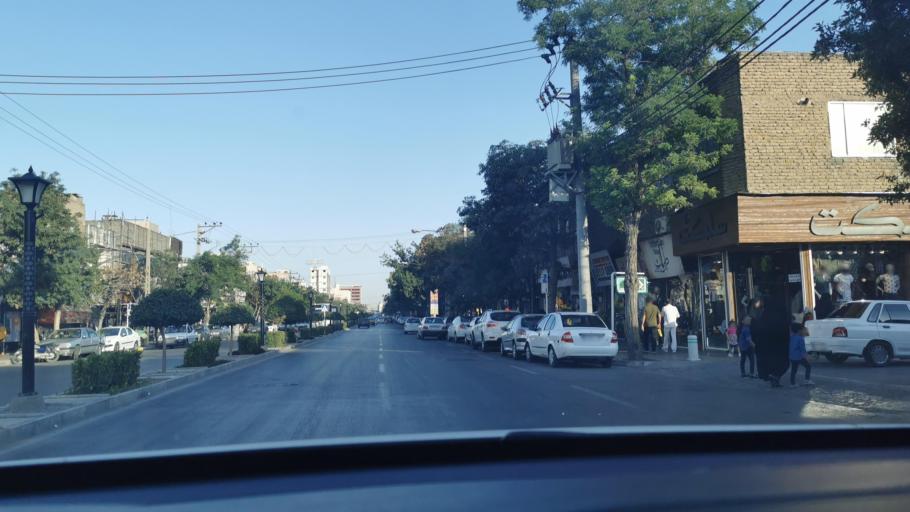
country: IR
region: Razavi Khorasan
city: Mashhad
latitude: 36.2972
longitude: 59.6422
